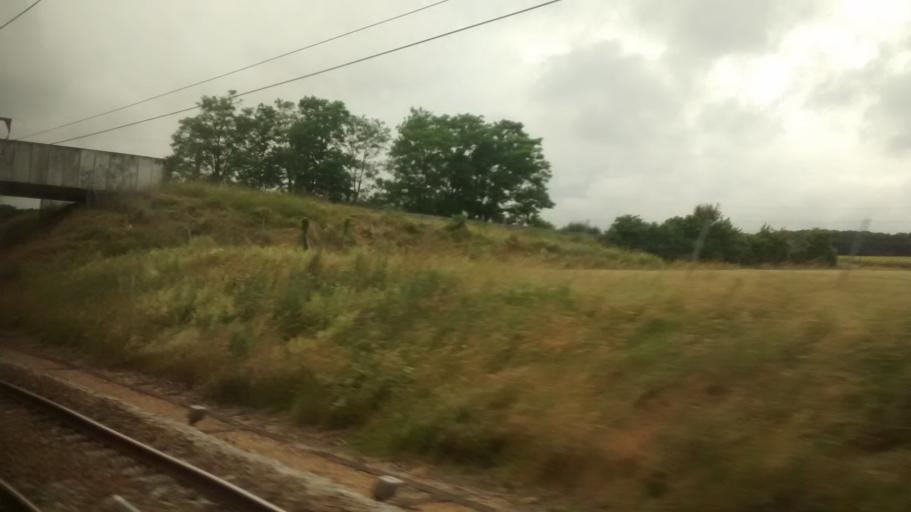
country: FR
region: Centre
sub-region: Departement d'Eure-et-Loir
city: La Bazoche-Gouet
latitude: 48.0855
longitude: 0.8950
